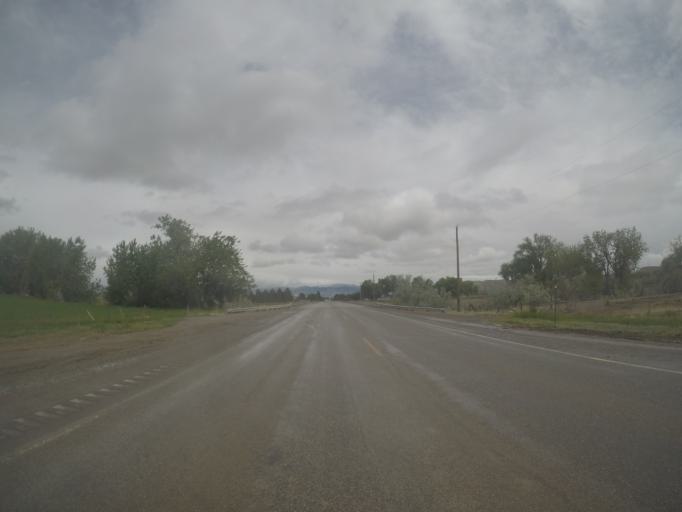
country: US
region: Wyoming
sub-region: Big Horn County
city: Lovell
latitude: 44.8406
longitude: -108.3538
